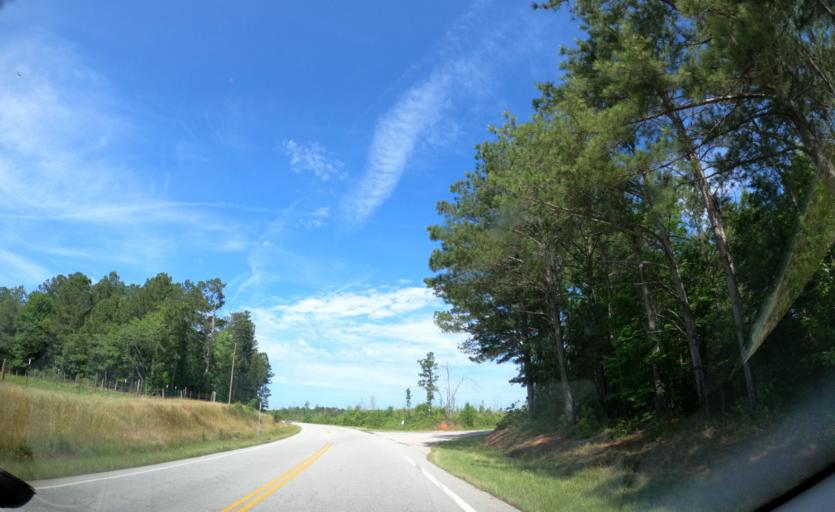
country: US
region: Georgia
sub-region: Elbert County
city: Elberton
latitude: 34.1589
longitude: -82.8317
